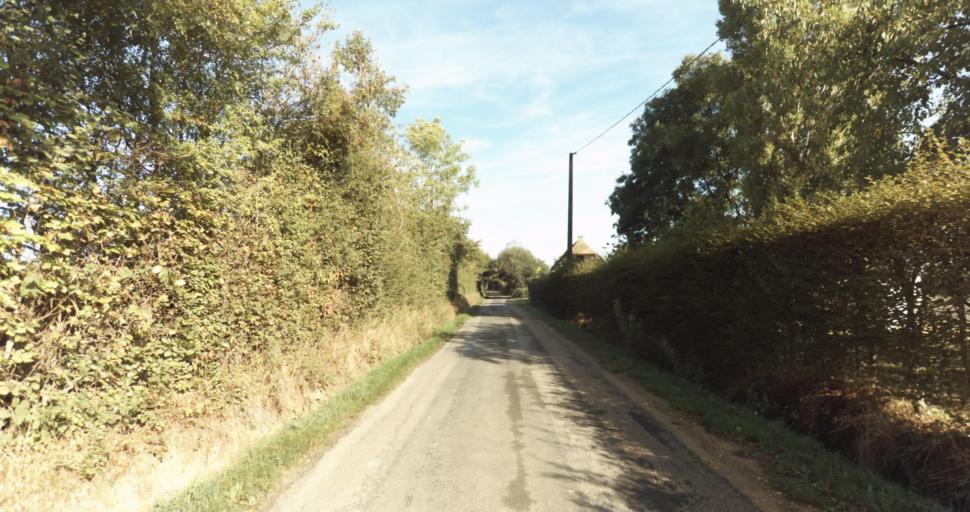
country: FR
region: Lower Normandy
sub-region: Departement de l'Orne
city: Vimoutiers
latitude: 48.9195
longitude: 0.2980
